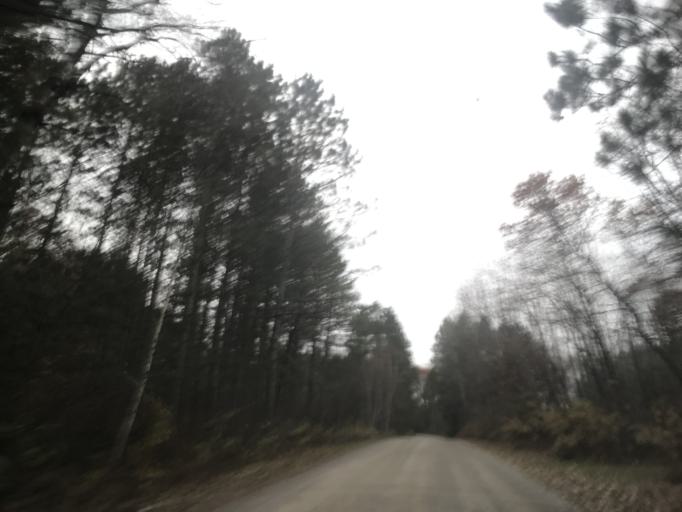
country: US
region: Wisconsin
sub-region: Oconto County
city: Gillett
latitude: 45.3510
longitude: -88.2836
